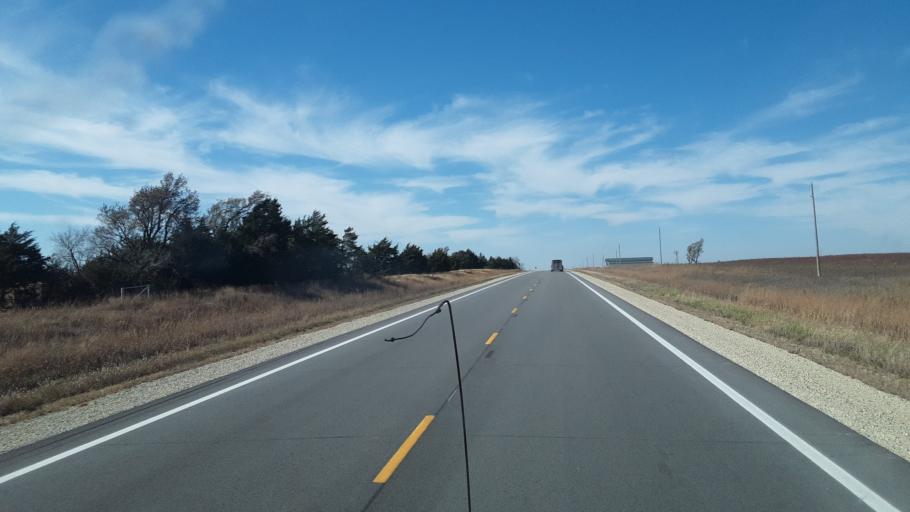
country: US
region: Kansas
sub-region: Marion County
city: Marion
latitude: 38.3629
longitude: -96.7953
